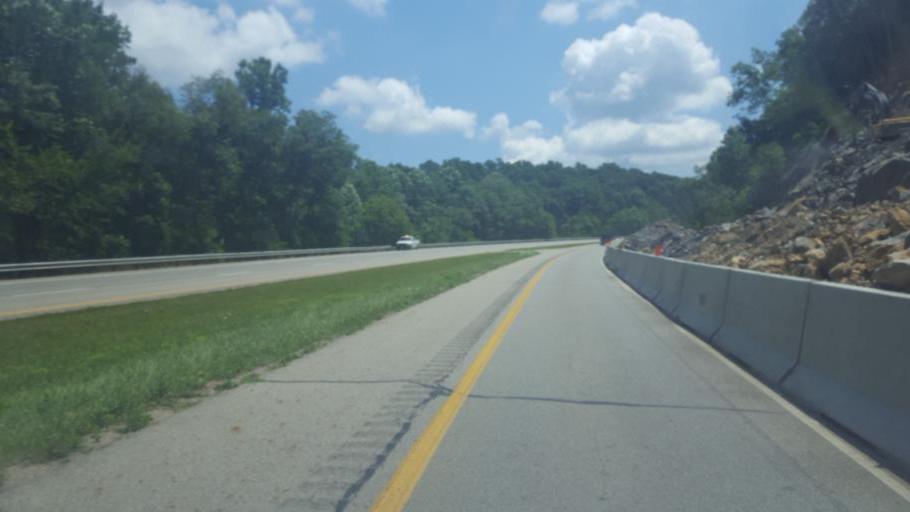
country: US
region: Ohio
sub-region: Jackson County
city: Jackson
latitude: 39.1213
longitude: -82.6931
